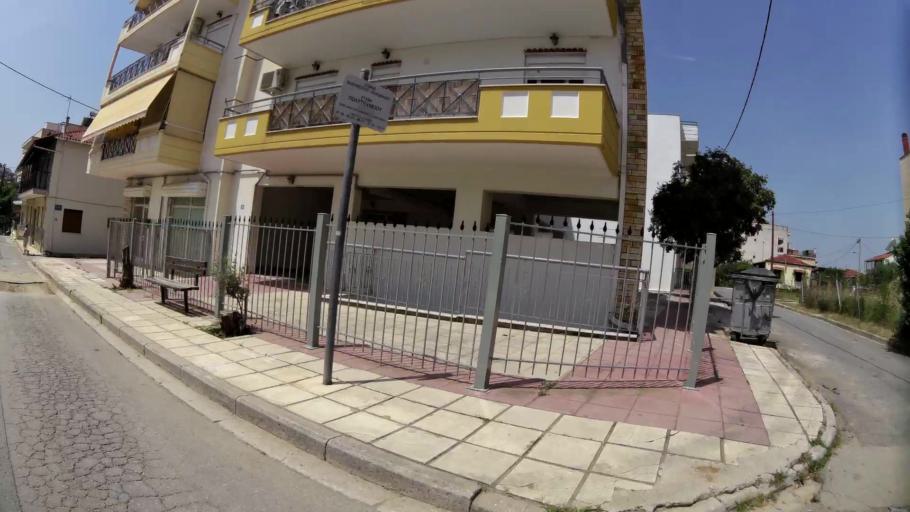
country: GR
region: Central Macedonia
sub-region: Nomos Thessalonikis
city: Evosmos
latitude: 40.6737
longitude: 22.8958
